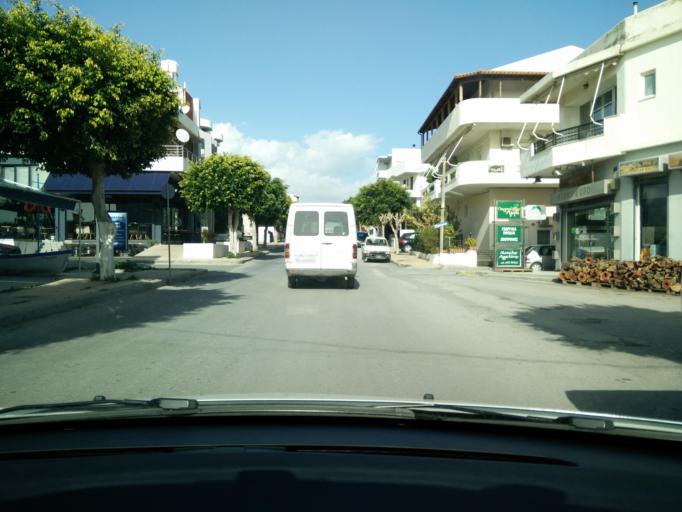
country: GR
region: Crete
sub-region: Nomos Lasithiou
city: Ierapetra
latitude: 35.0106
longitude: 25.7358
